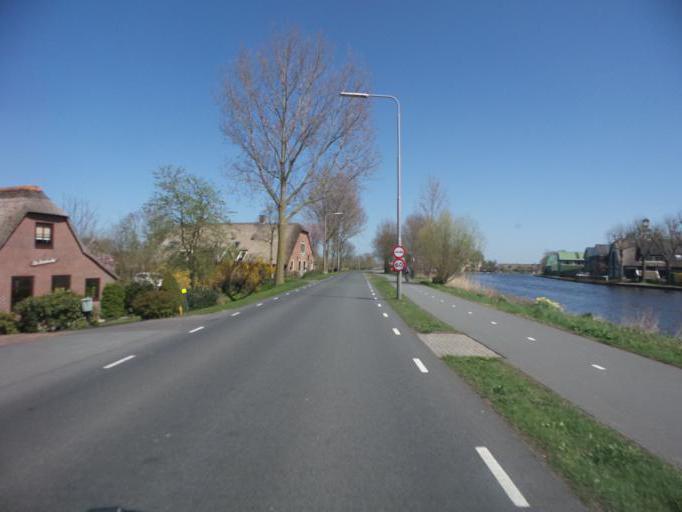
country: NL
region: South Holland
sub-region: Bodegraven-Reeuwijk
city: Bodegraven
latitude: 52.0859
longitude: 4.7909
